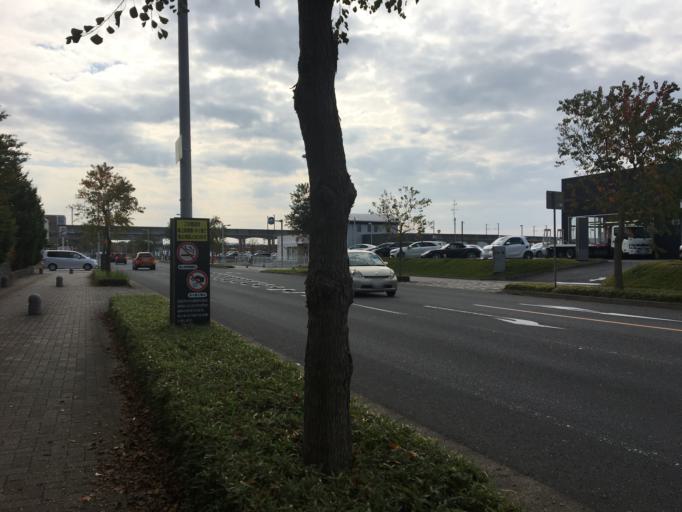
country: JP
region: Ibaraki
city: Naka
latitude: 36.0845
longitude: 140.0799
